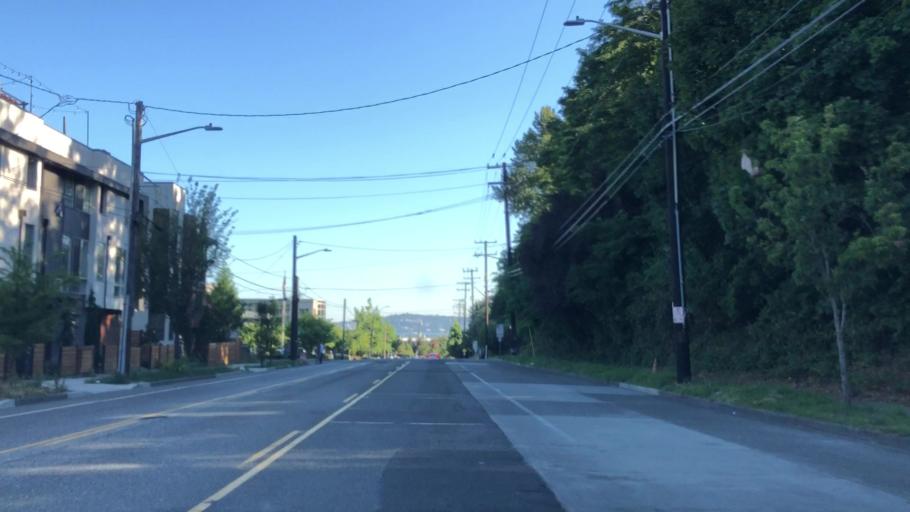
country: US
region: Washington
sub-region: King County
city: White Center
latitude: 47.5659
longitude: -122.3633
